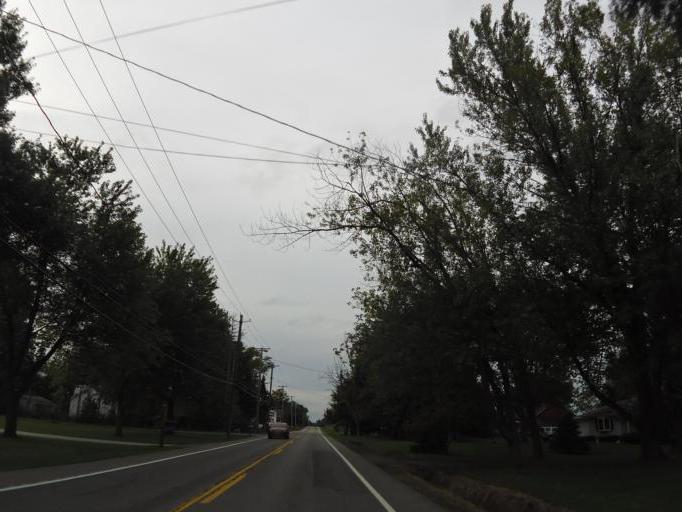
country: US
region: New York
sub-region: Erie County
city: Elma Center
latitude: 42.8128
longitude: -78.6367
